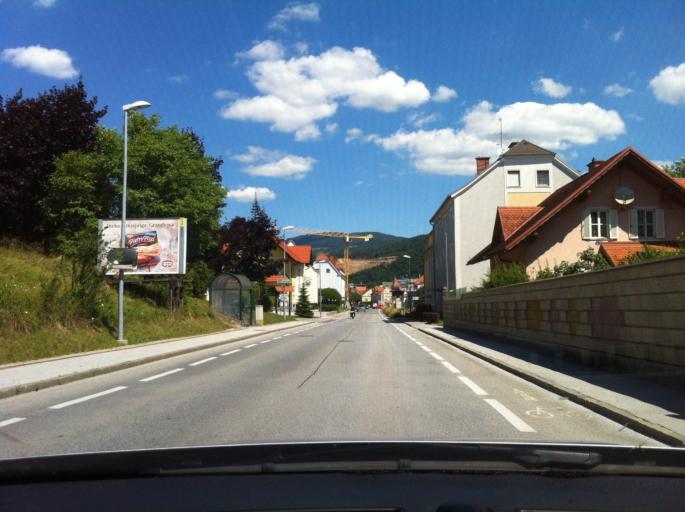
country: AT
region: Styria
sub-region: Politischer Bezirk Weiz
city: Weiz
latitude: 47.2109
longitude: 15.6259
